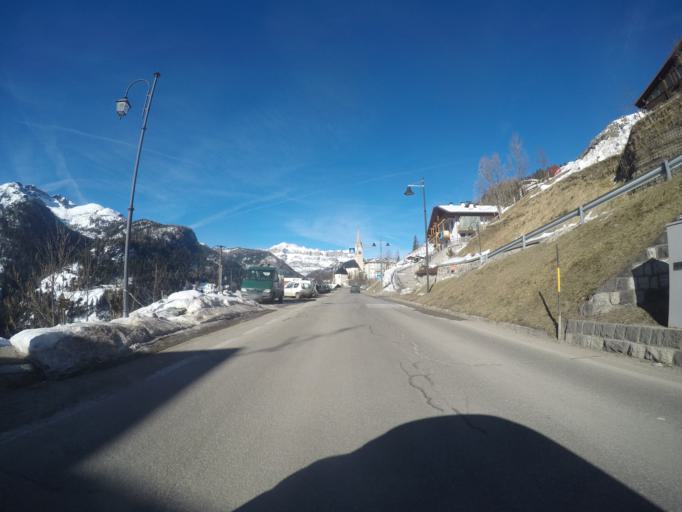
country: IT
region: Veneto
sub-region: Provincia di Belluno
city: Livinallongo del Col di Lana
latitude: 46.4801
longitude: 11.9573
